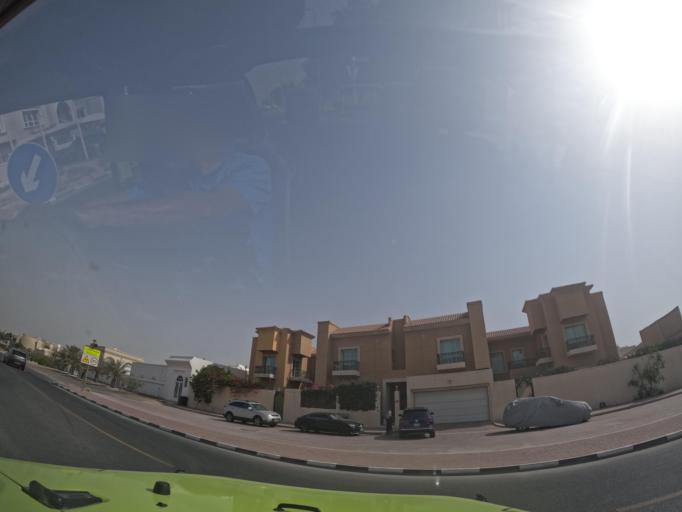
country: AE
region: Dubai
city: Dubai
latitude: 25.1470
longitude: 55.2140
